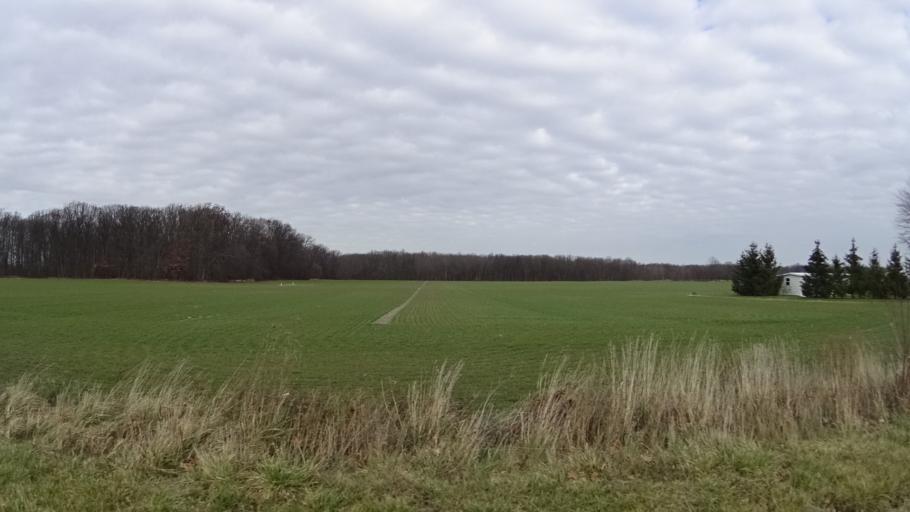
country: US
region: Ohio
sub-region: Lorain County
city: Camden
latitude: 41.1970
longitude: -82.3531
